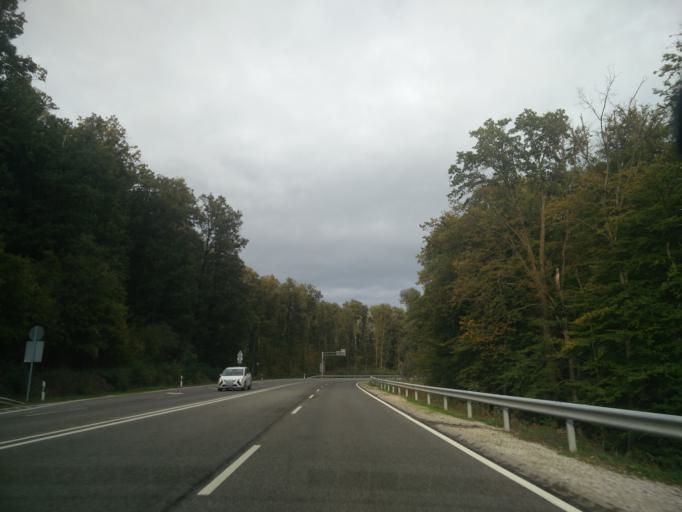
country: HU
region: Zala
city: Zalaegerszeg
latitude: 46.8271
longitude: 16.9614
